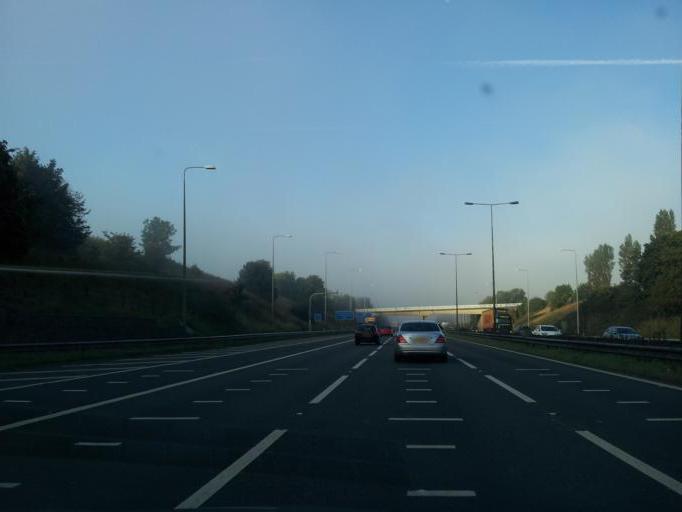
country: GB
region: England
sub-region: City and Borough of Leeds
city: Drighlington
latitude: 53.7447
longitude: -1.6593
